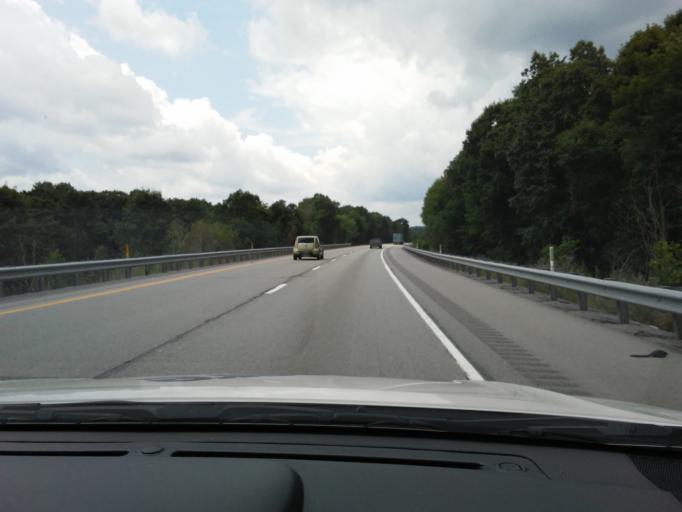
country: US
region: Pennsylvania
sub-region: Clearfield County
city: Troy
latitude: 40.9861
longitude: -78.1865
